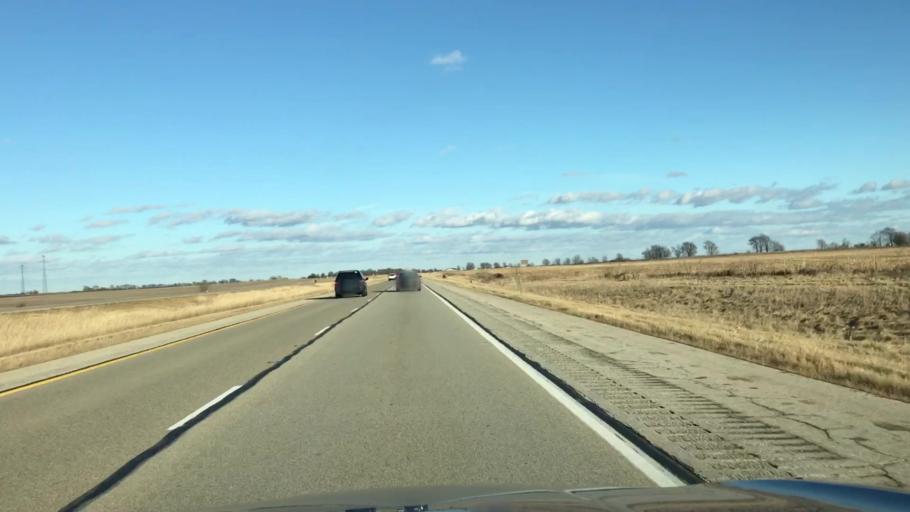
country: US
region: Illinois
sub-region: McLean County
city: Lexington
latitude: 40.5850
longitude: -88.8751
